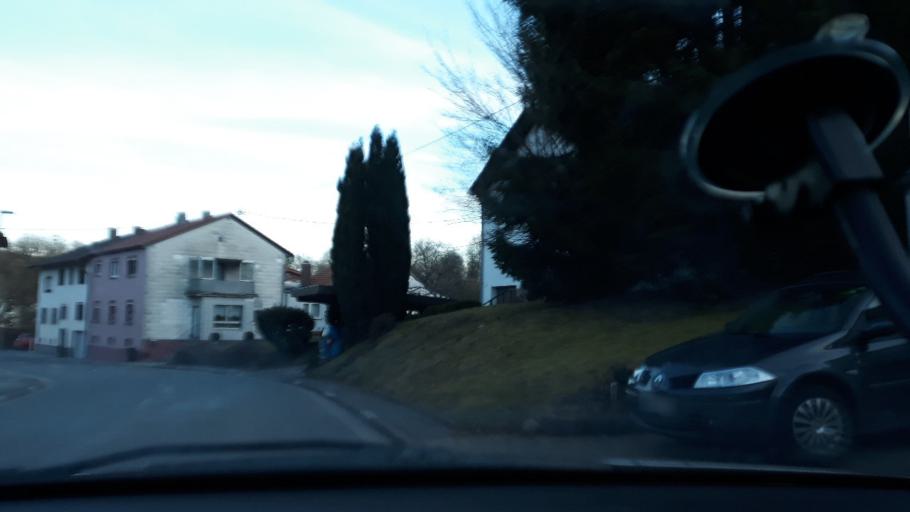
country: DE
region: Saarland
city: Sankt Ingbert
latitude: 49.2252
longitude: 7.1421
